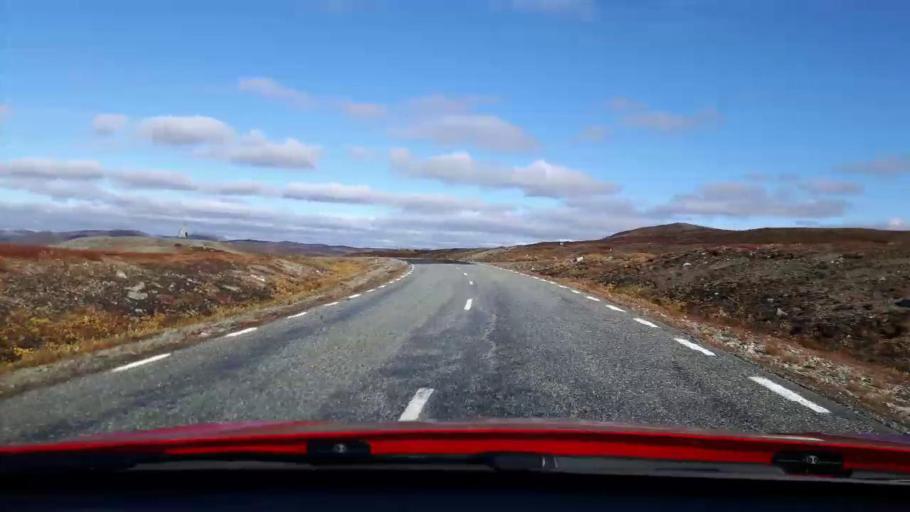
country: NO
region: Nordland
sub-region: Hattfjelldal
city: Hattfjelldal
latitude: 65.0862
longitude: 14.4575
